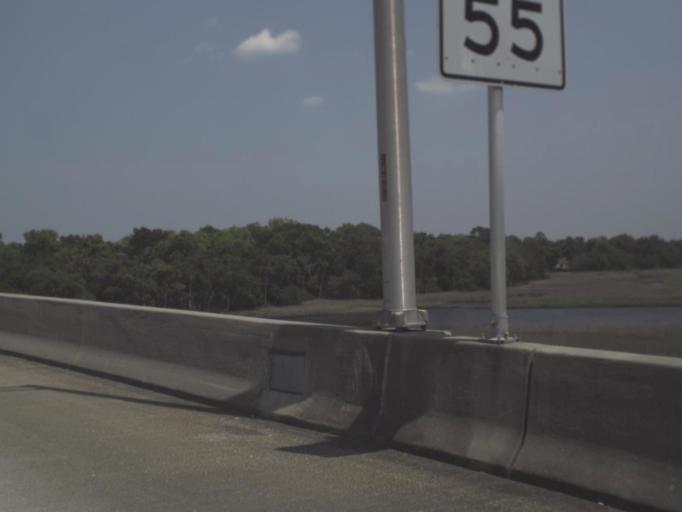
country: US
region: Florida
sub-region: Duval County
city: Atlantic Beach
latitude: 30.3581
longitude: -81.4606
